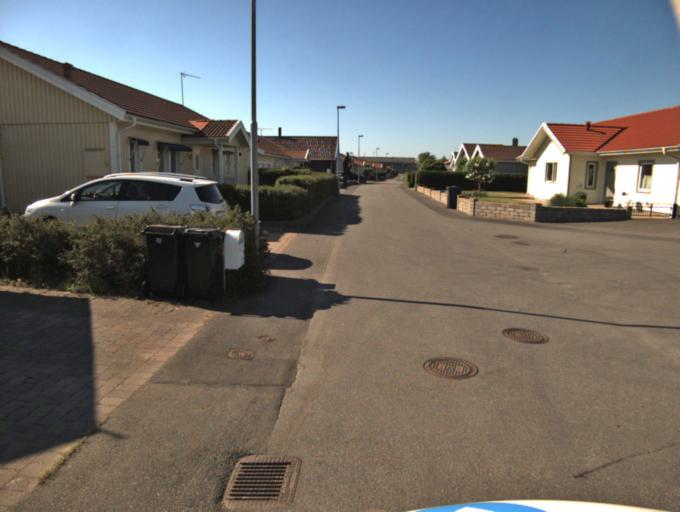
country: SE
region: Skane
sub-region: Kristianstads Kommun
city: Kristianstad
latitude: 56.0306
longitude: 14.2064
